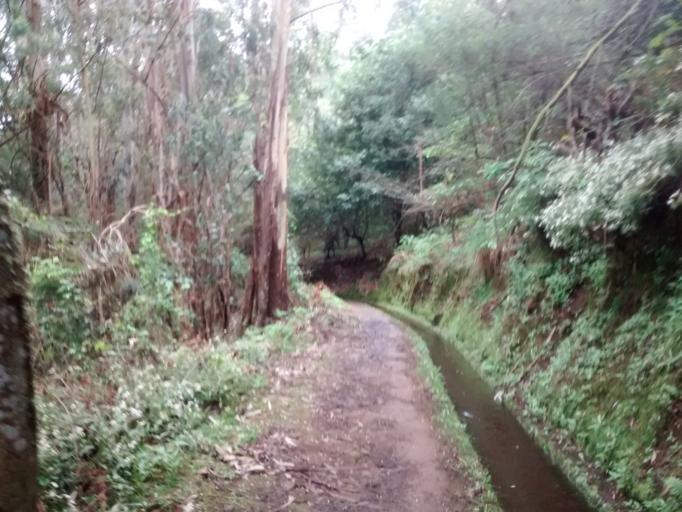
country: PT
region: Madeira
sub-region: Santana
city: Santana
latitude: 32.8125
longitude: -16.9278
